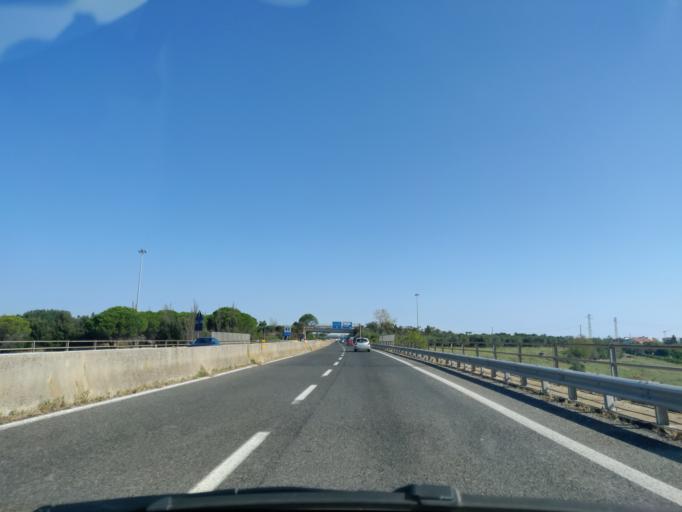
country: IT
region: Latium
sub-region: Provincia di Viterbo
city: Viterbo
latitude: 42.4164
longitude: 12.0772
